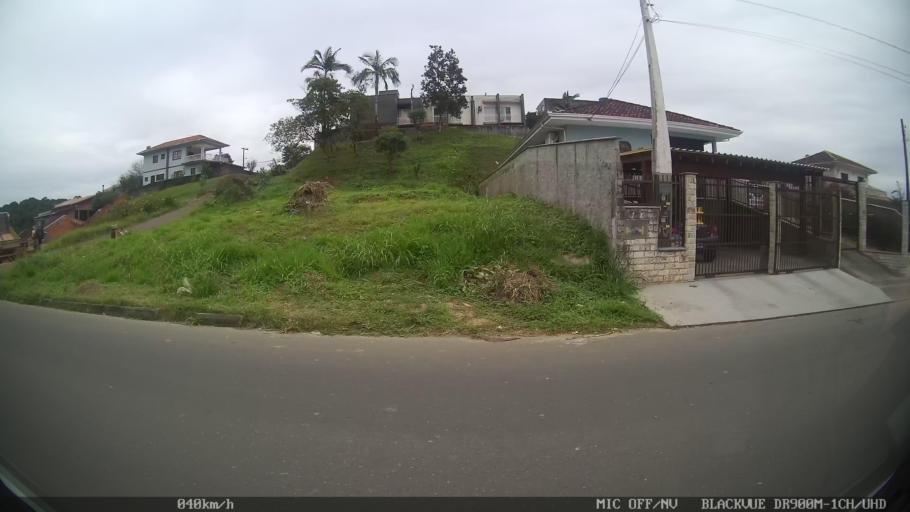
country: BR
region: Santa Catarina
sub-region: Joinville
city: Joinville
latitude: -26.2693
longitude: -48.8835
